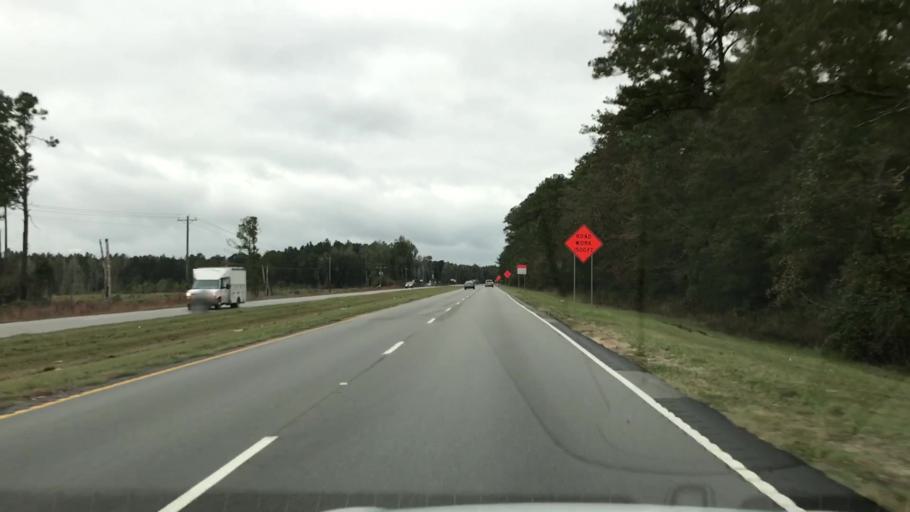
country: US
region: South Carolina
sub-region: Georgetown County
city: Georgetown
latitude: 33.2885
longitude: -79.3482
